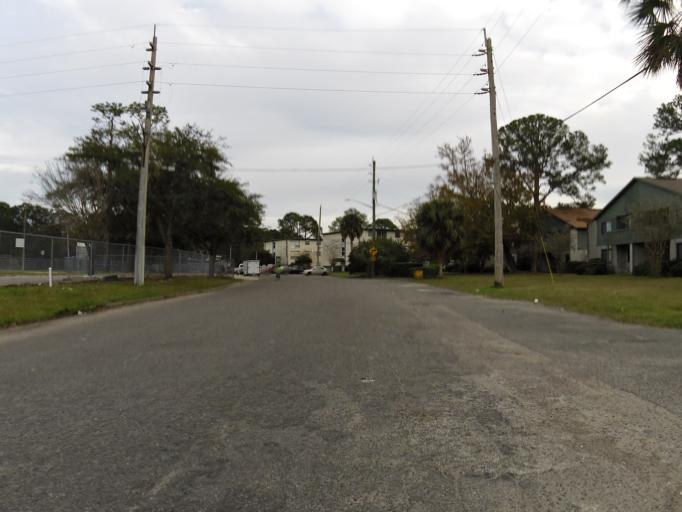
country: US
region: Florida
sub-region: Duval County
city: Jacksonville
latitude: 30.2494
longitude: -81.6326
